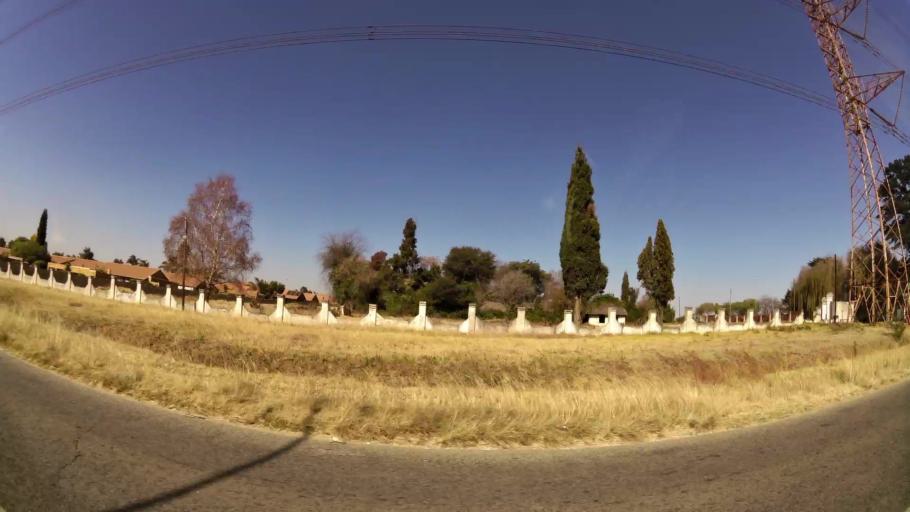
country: ZA
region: Gauteng
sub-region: City of Johannesburg Metropolitan Municipality
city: Modderfontein
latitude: -26.0757
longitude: 28.1984
